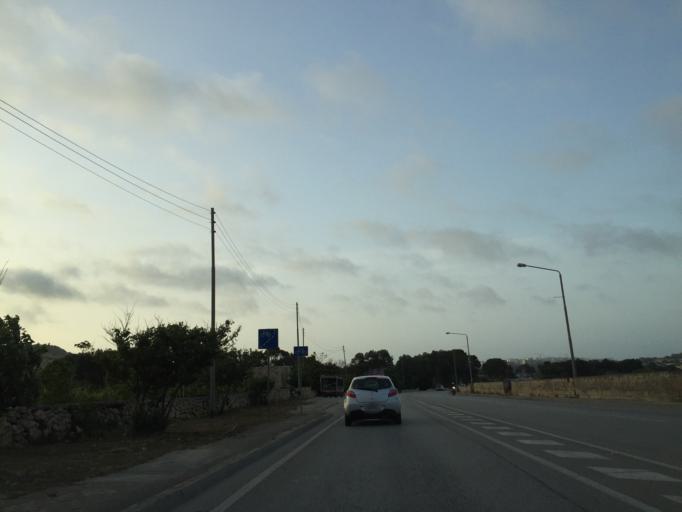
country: MT
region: Il-Mosta
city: Mosta
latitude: 35.9217
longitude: 14.4155
